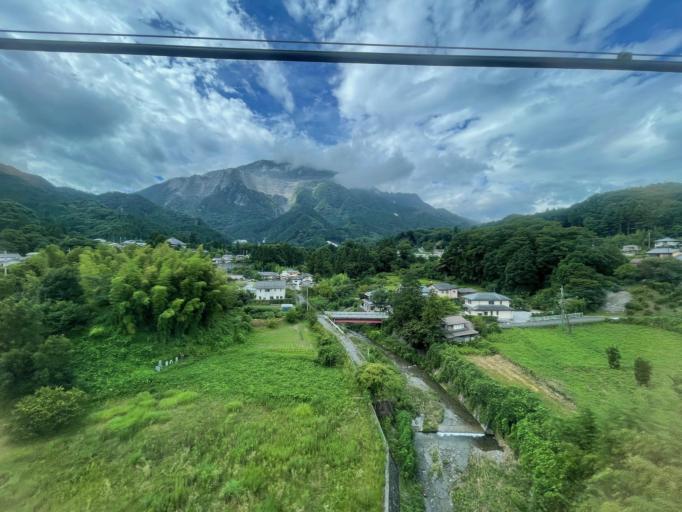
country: JP
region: Saitama
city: Chichibu
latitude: 35.9746
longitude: 139.1205
